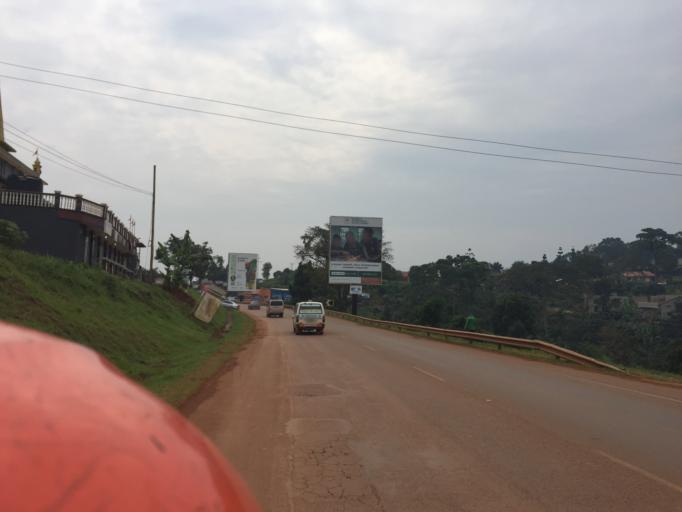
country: UG
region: Central Region
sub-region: Wakiso District
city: Kajansi
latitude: 0.1660
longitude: 32.5431
